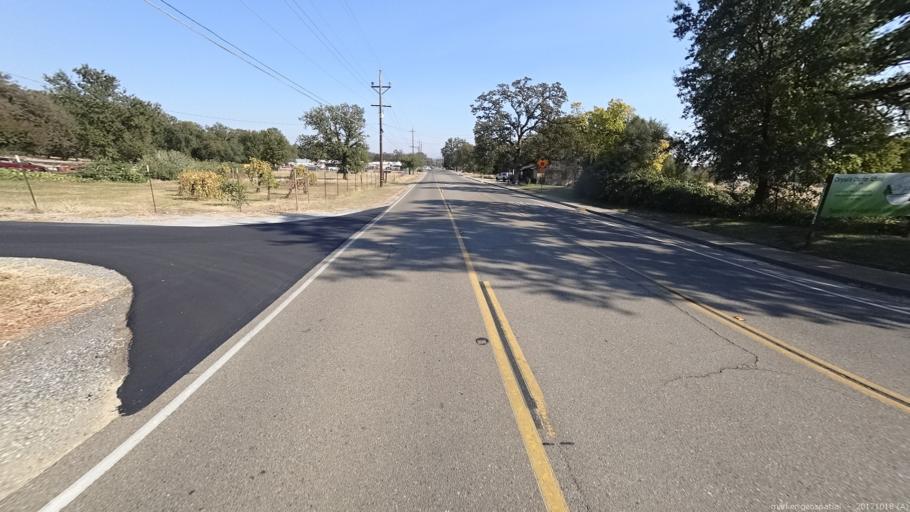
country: US
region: California
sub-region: Shasta County
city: Palo Cedro
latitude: 40.5638
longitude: -122.2417
